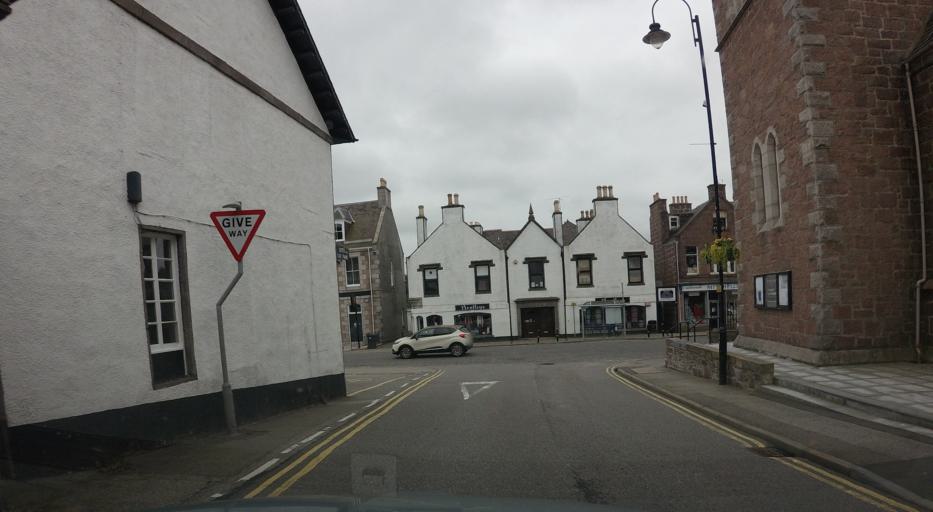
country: GB
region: Scotland
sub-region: Aberdeenshire
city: Banchory
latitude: 57.0517
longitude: -2.5050
